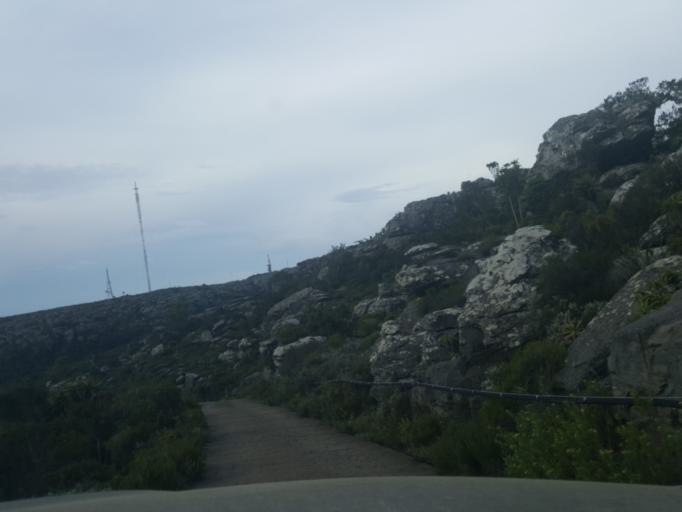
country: ZA
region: Limpopo
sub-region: Mopani District Municipality
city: Hoedspruit
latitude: -24.5514
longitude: 30.8693
